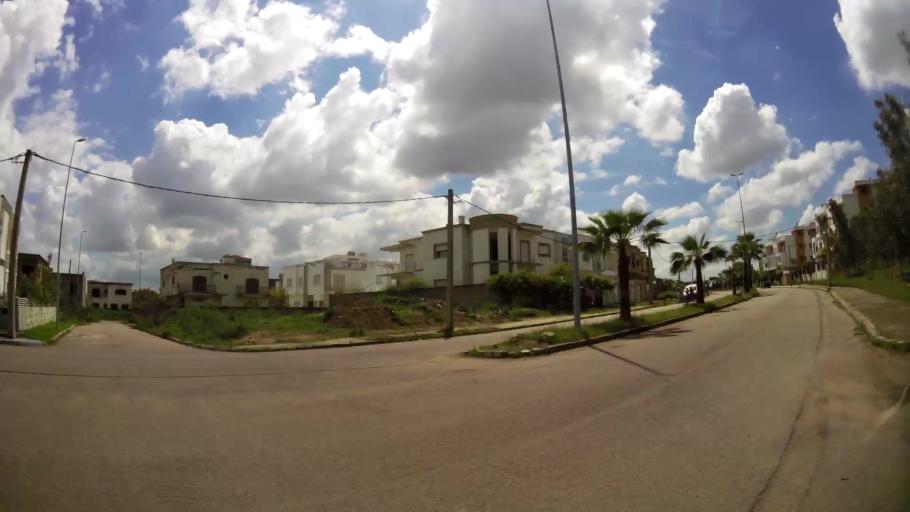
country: MA
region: Chaouia-Ouardigha
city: Nouaseur
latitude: 33.3989
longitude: -7.5641
